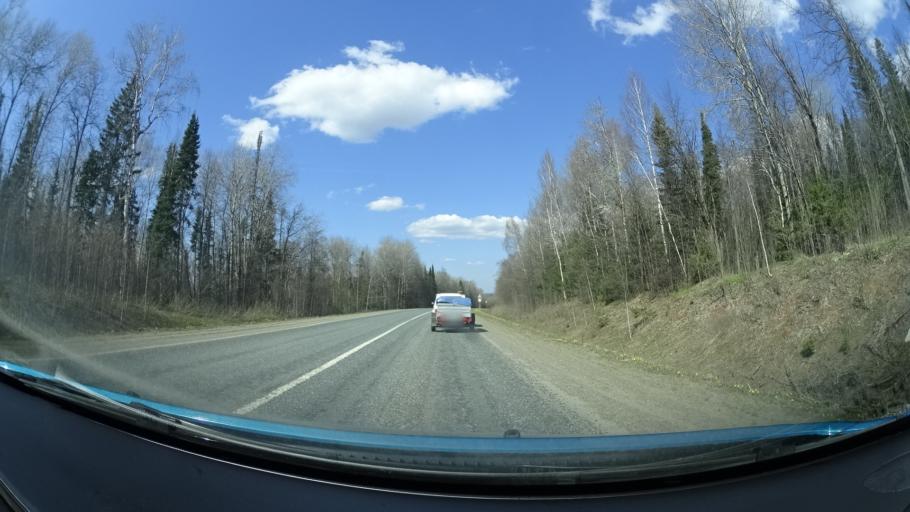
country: RU
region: Perm
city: Yugo-Kamskiy
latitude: 57.6247
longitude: 55.6183
